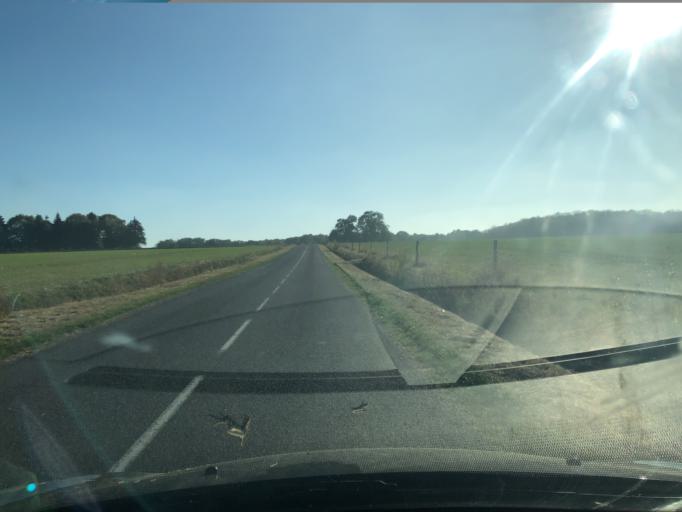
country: FR
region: Centre
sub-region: Departement d'Indre-et-Loire
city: Neuvy-le-Roi
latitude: 47.5951
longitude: 0.5959
